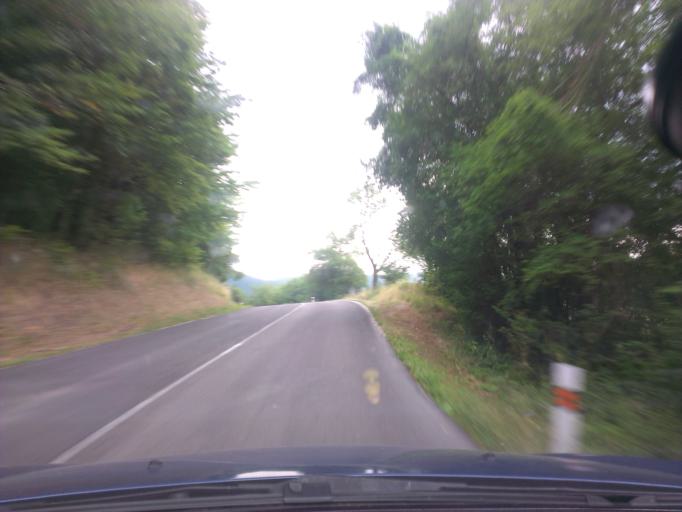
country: SK
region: Trnavsky
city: Vrbove
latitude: 48.6689
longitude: 17.6930
